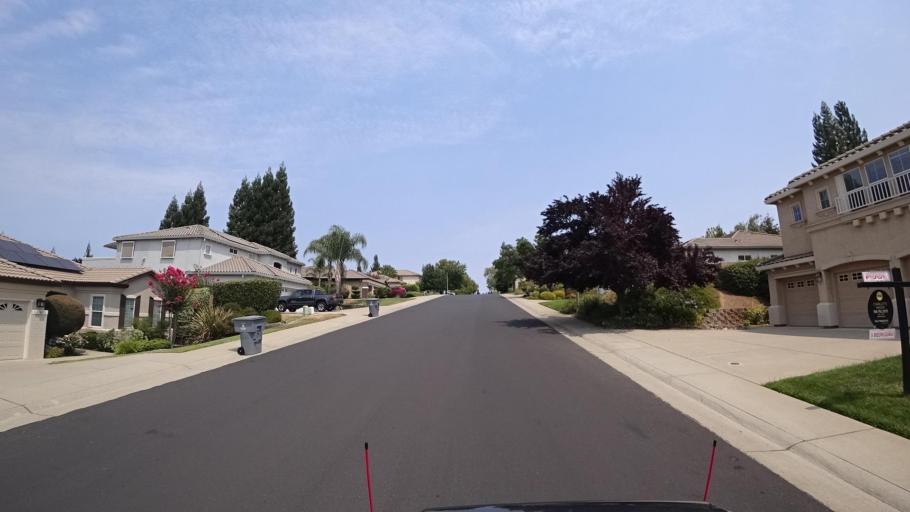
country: US
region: California
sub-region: Placer County
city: Rocklin
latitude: 38.7736
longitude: -121.2205
